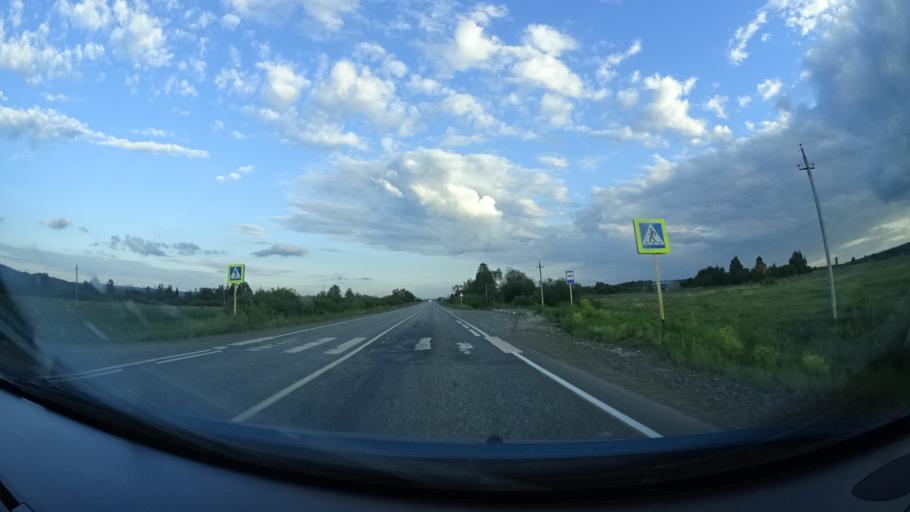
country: RU
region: Perm
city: Barda
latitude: 56.9714
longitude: 55.5778
